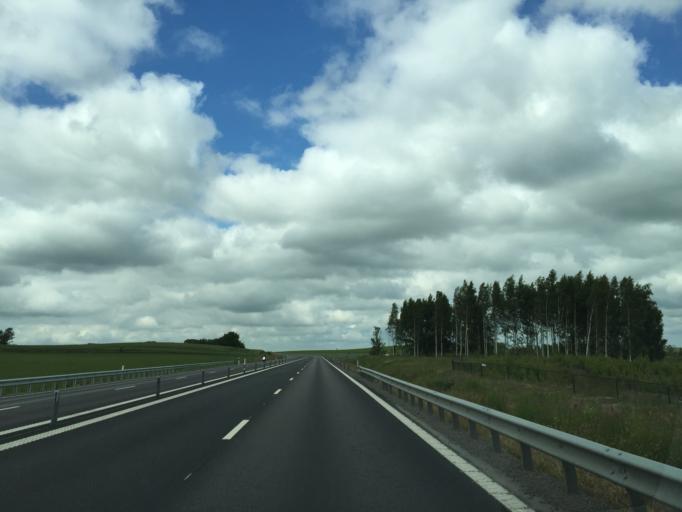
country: SE
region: Skane
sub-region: Svedala Kommun
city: Klagerup
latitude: 55.5661
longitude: 13.2557
